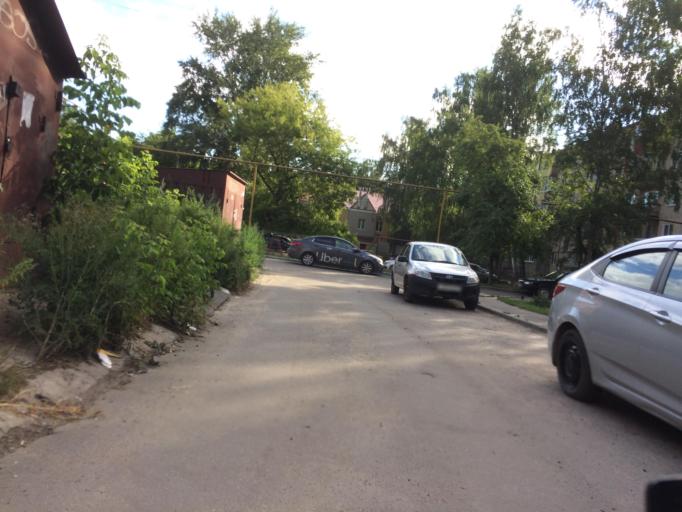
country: RU
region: Mariy-El
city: Yoshkar-Ola
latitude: 56.6244
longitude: 47.8806
